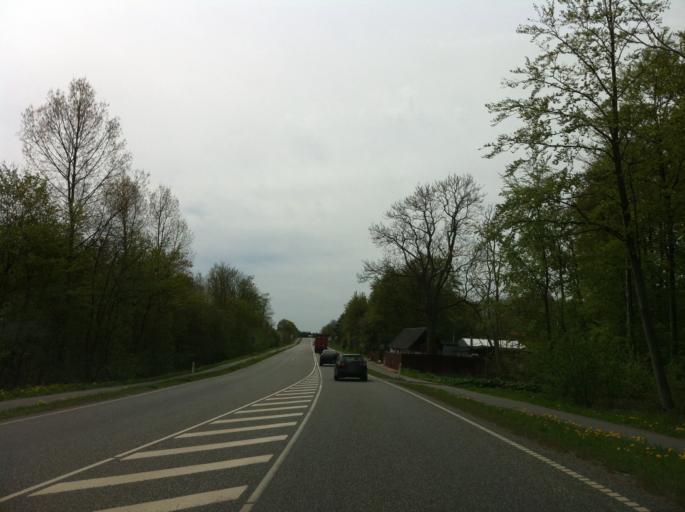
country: DK
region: Zealand
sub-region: Lejre Kommune
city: Osted
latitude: 55.5121
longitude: 11.8914
